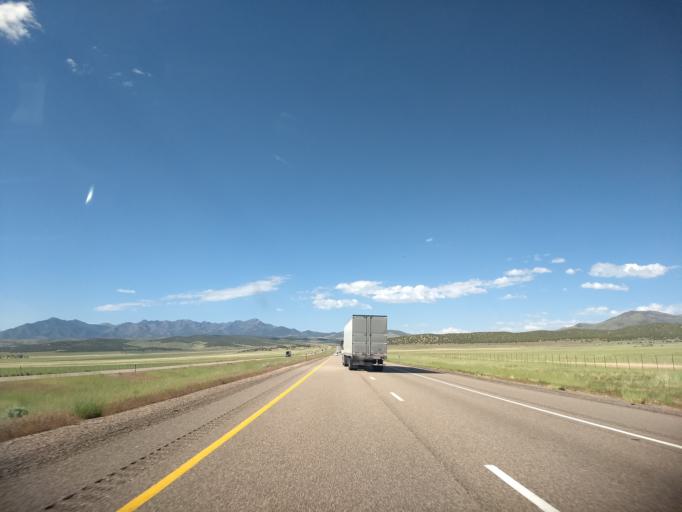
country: US
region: Utah
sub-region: Millard County
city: Fillmore
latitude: 39.1161
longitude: -112.2507
